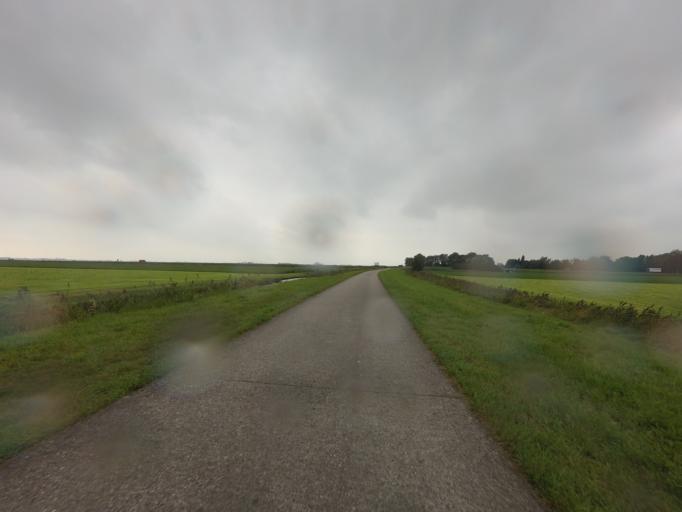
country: NL
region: Friesland
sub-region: Sudwest Fryslan
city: Koudum
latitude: 52.9470
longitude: 5.4403
